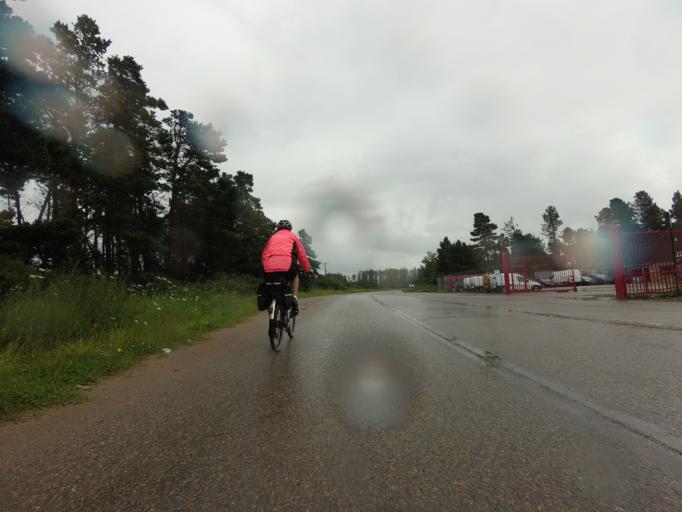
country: GB
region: Scotland
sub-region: Moray
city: Fochabers
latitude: 57.6619
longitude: -3.0607
